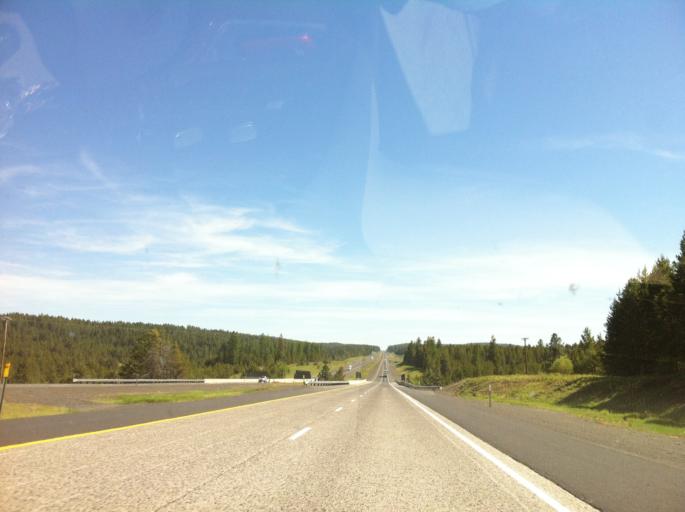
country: US
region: Oregon
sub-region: Umatilla County
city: Mission
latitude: 45.5187
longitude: -118.4375
